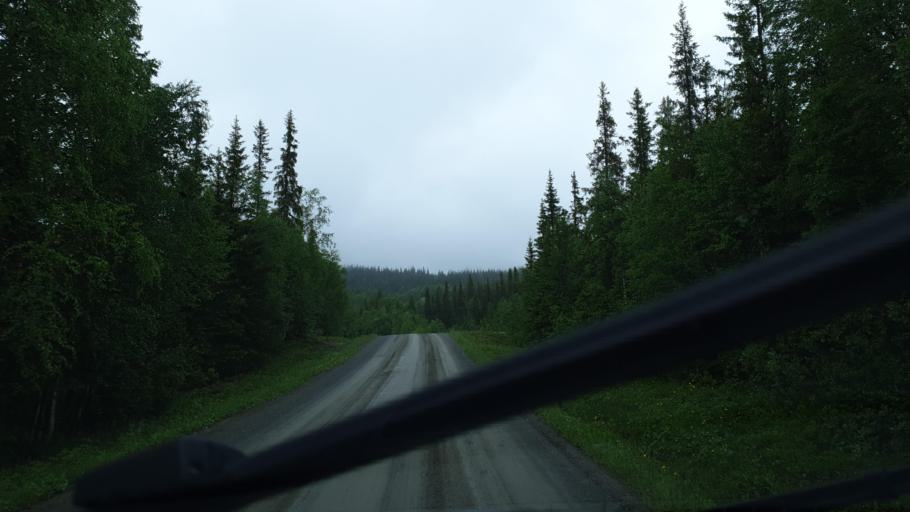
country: SE
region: Vaesterbotten
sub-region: Vilhelmina Kommun
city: Sjoberg
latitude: 65.3412
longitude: 15.8712
